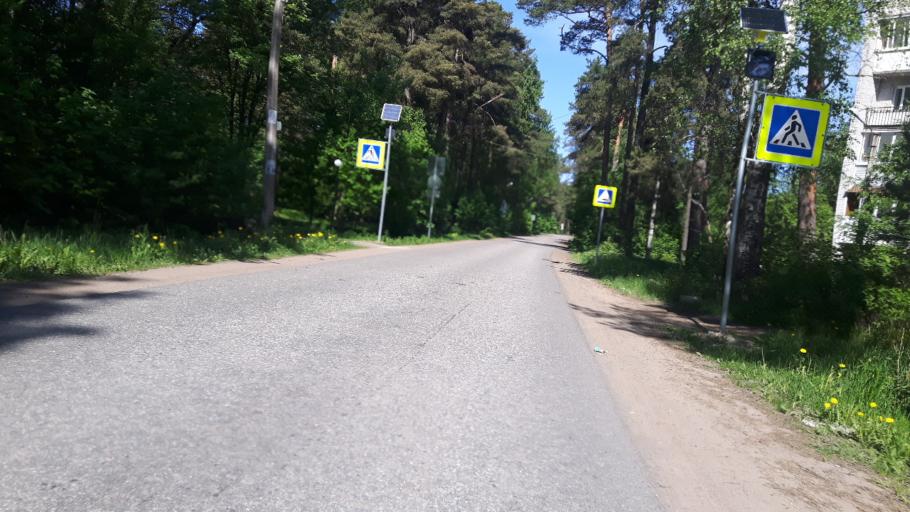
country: RU
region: Leningrad
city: Lebyazh'ye
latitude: 59.9626
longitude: 29.4121
